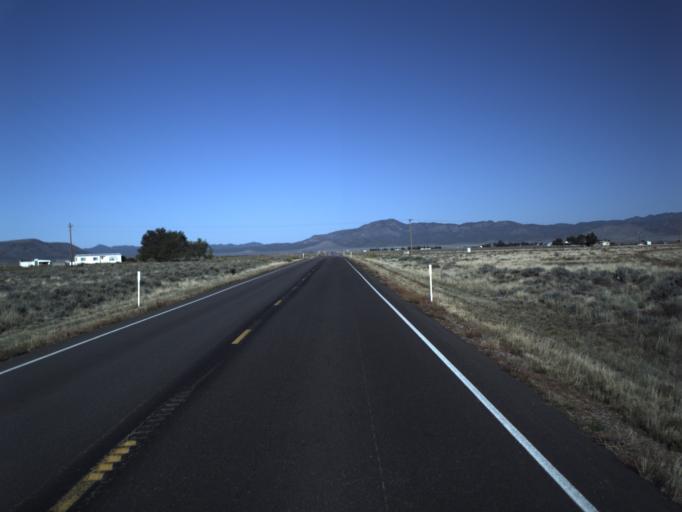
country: US
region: Utah
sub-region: Washington County
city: Enterprise
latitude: 37.7542
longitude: -113.7818
